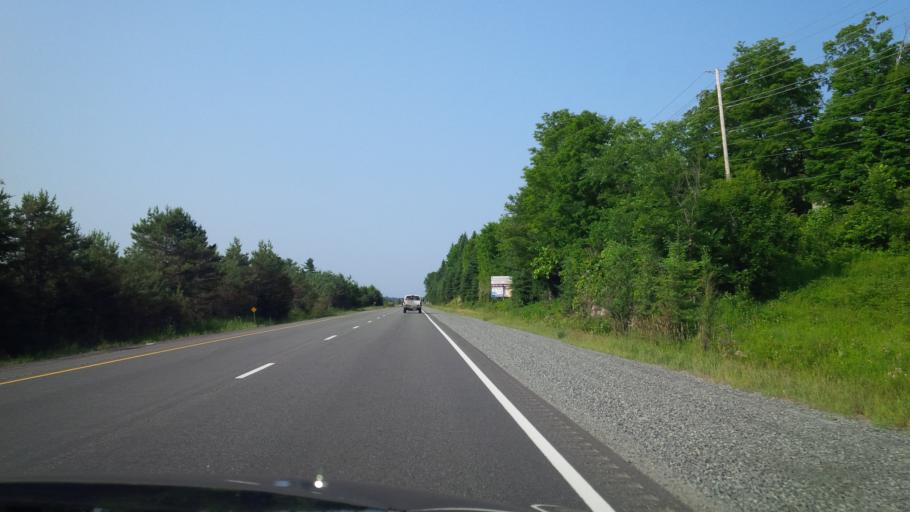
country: CA
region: Ontario
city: Huntsville
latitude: 45.2810
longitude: -79.2769
